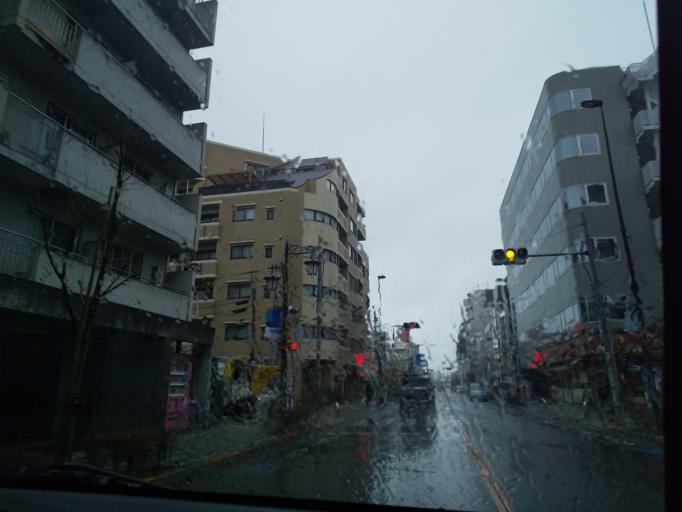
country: JP
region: Tokyo
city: Hino
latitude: 35.6943
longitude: 139.4160
